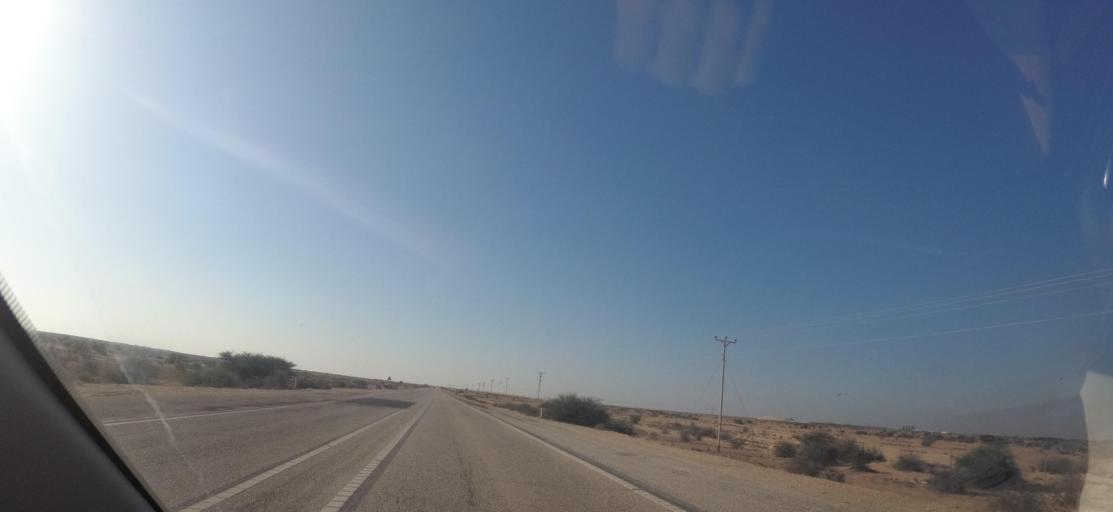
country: QA
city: Al Ghuwayriyah
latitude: 25.8565
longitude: 51.2538
